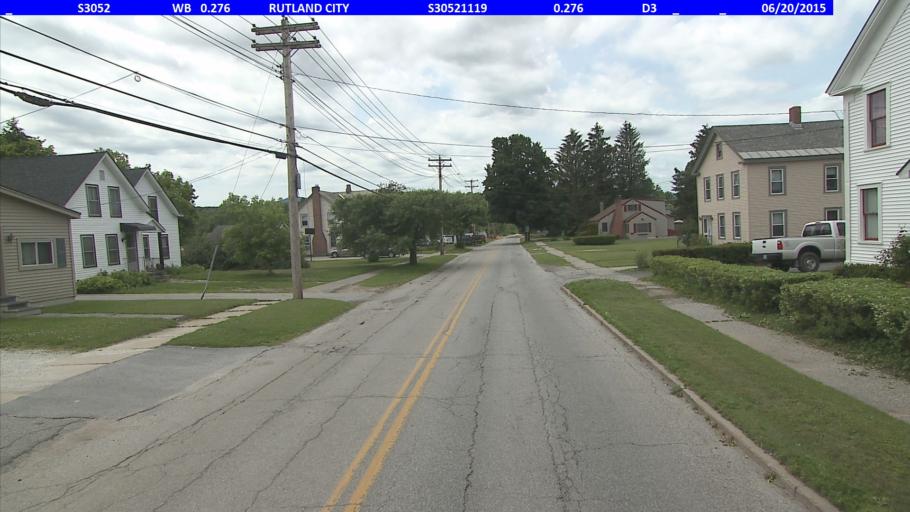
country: US
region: Vermont
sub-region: Rutland County
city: Rutland
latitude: 43.6011
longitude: -72.9874
